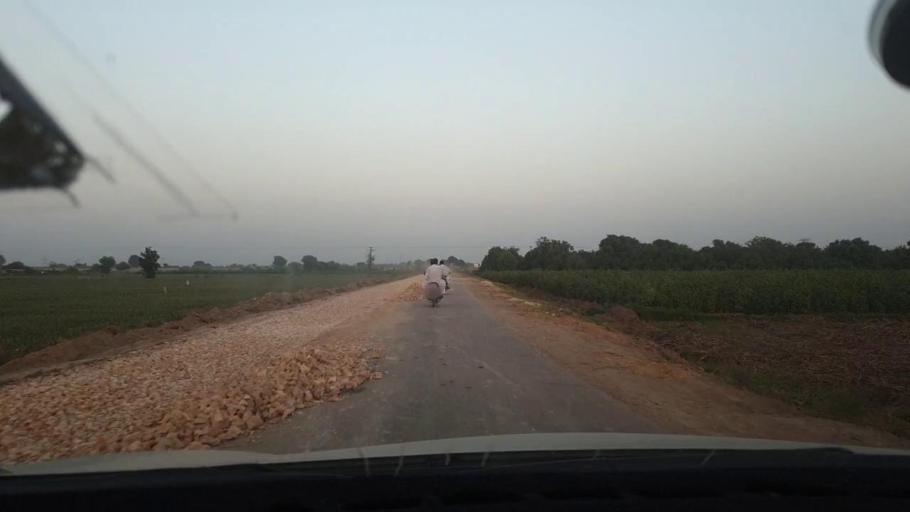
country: PK
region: Sindh
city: Bhit Shah
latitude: 25.7528
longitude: 68.5405
